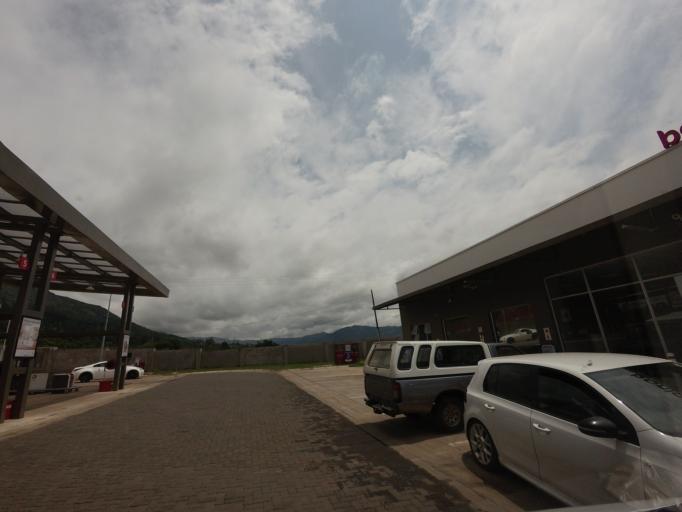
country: SZ
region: Hhohho
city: Lobamba
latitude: -26.4316
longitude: 31.1840
